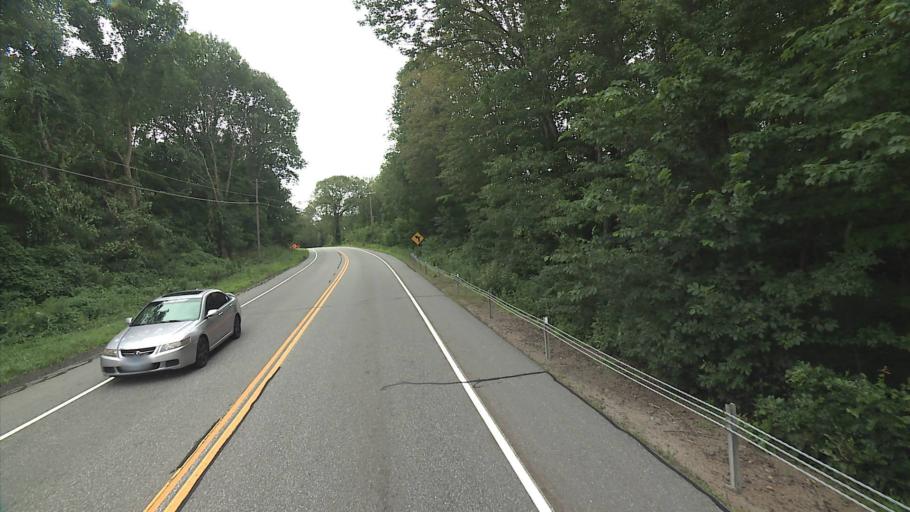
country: US
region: Connecticut
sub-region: Tolland County
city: Storrs
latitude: 41.8737
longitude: -72.2233
